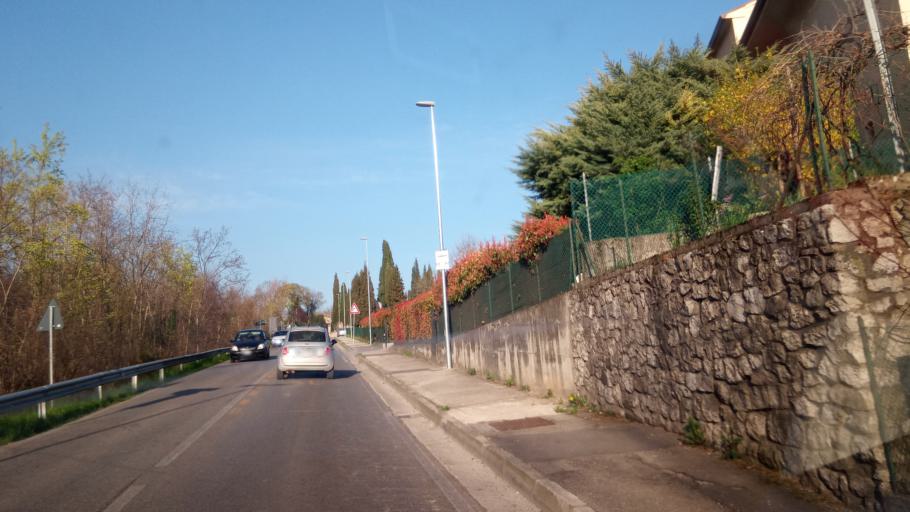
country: IT
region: Veneto
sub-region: Provincia di Treviso
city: Crespano del Grappa
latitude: 45.8188
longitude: 11.8172
